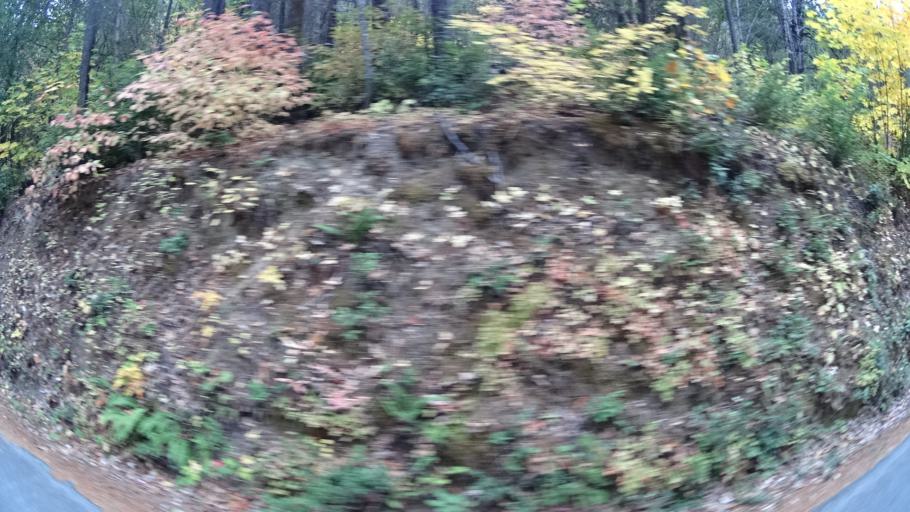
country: US
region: California
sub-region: Siskiyou County
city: Happy Camp
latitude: 41.7829
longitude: -123.3096
